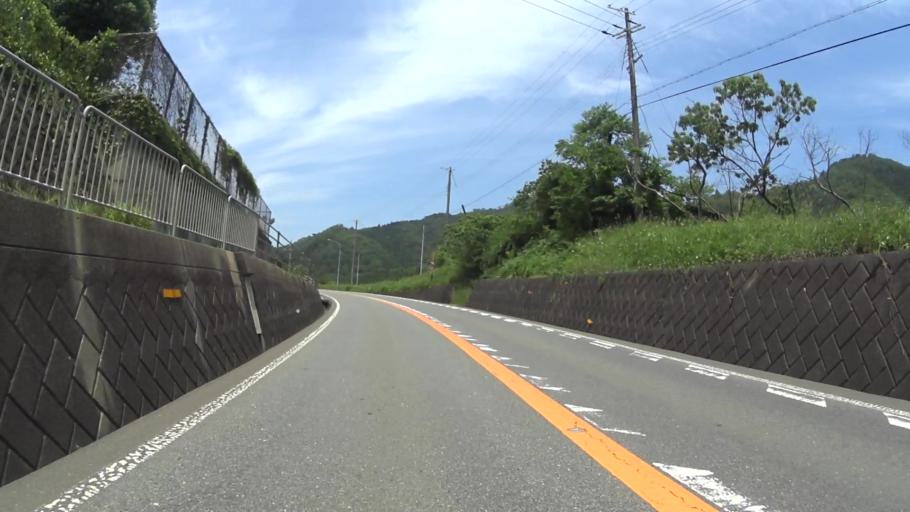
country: JP
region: Kyoto
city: Ayabe
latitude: 35.2063
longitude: 135.2468
